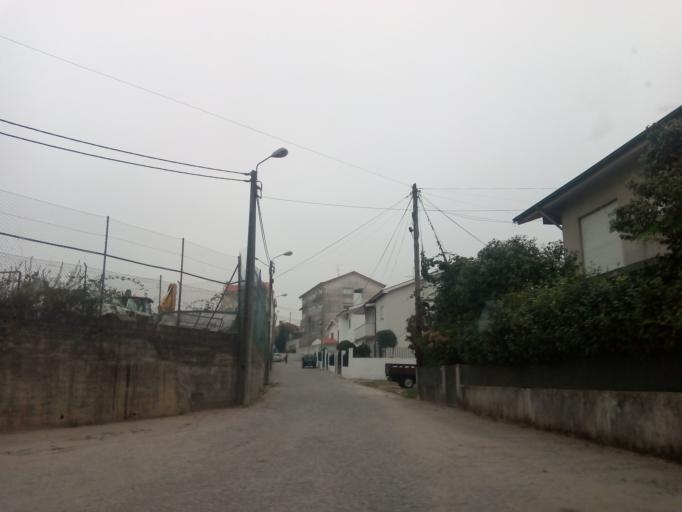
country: PT
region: Porto
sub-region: Paredes
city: Casteloes de Cepeda
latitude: 41.2000
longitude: -8.3408
